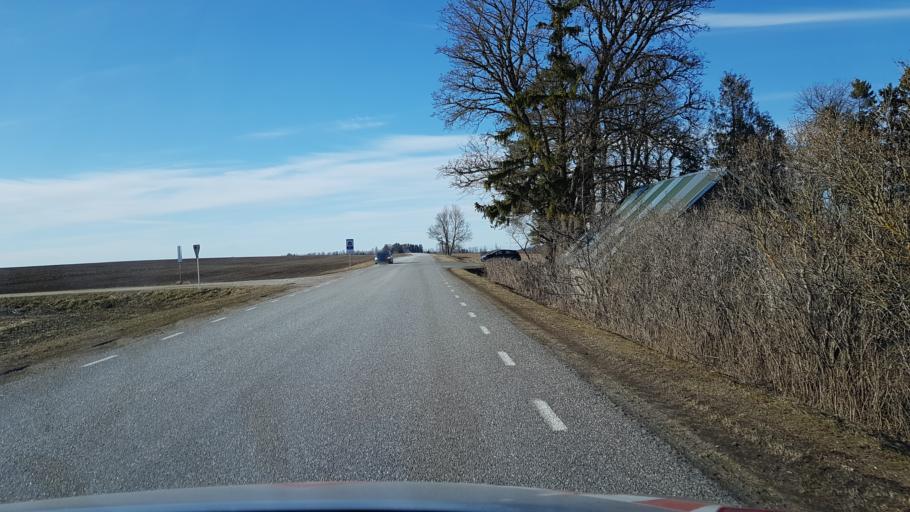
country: EE
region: Laeaene-Virumaa
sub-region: Kadrina vald
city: Kadrina
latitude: 59.3253
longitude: 26.1405
